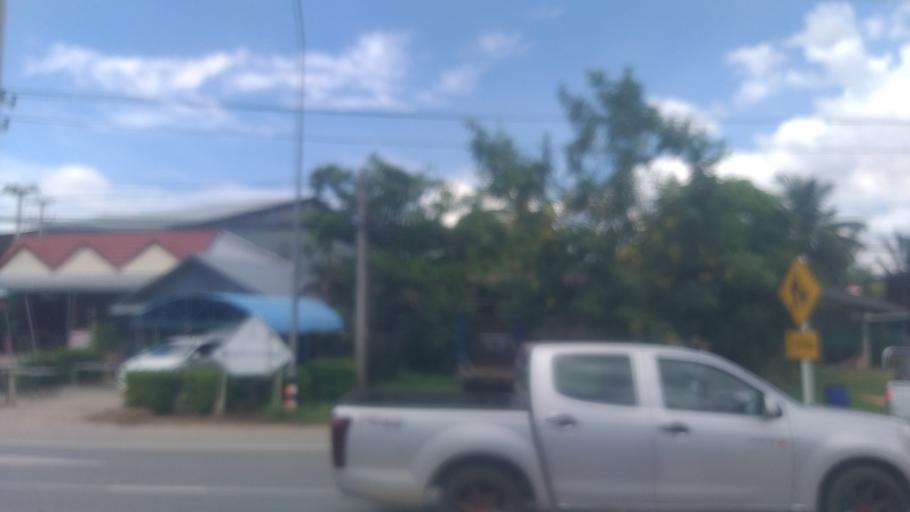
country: TH
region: Nakhon Ratchasima
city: Phra Thong Kham
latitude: 15.2636
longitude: 102.0232
